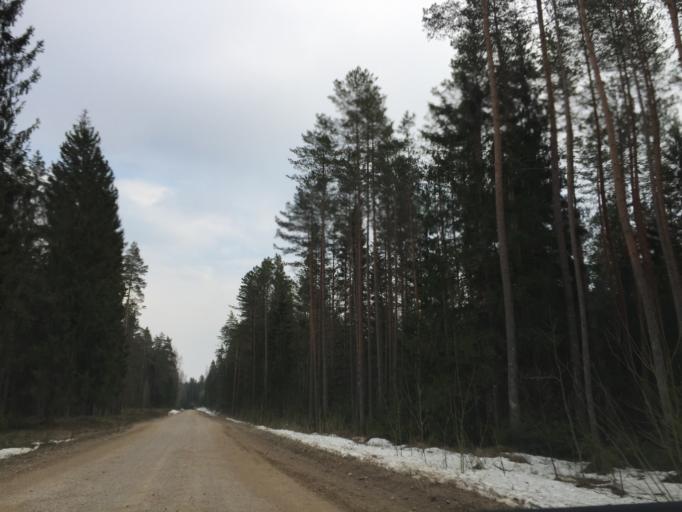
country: LV
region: Raunas
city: Rauna
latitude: 57.1552
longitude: 25.5483
